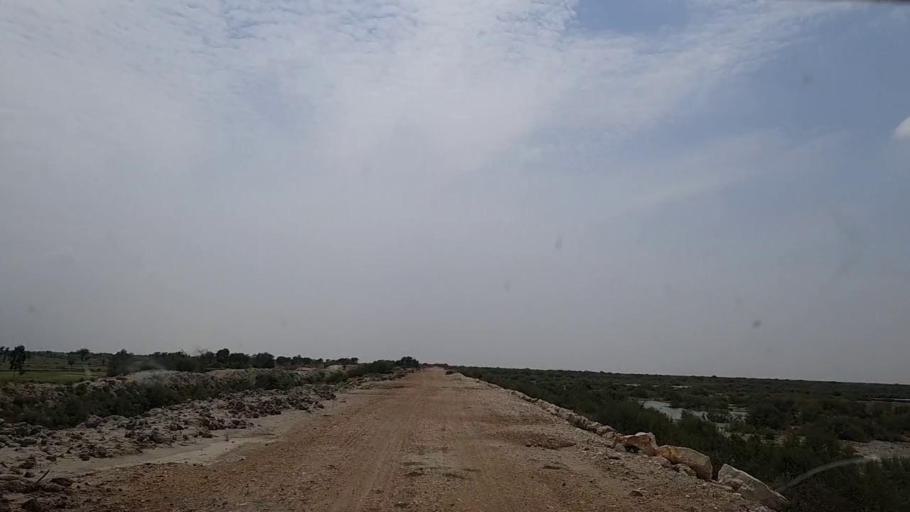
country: PK
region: Sindh
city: Phulji
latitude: 26.8566
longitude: 67.6305
